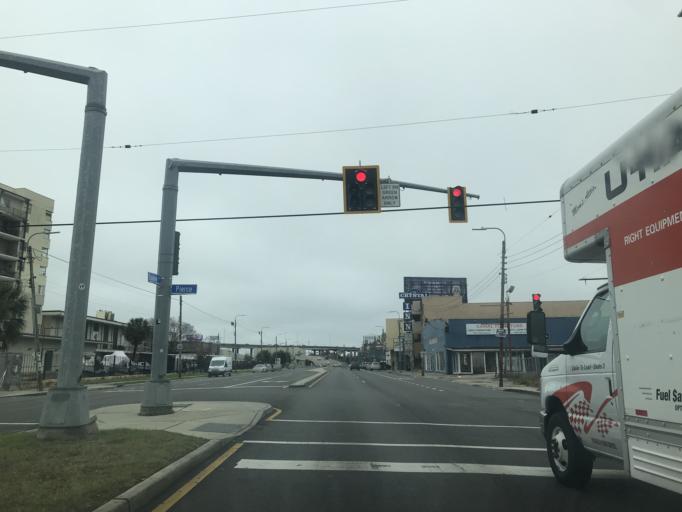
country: US
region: Louisiana
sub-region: Orleans Parish
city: New Orleans
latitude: 29.9680
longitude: -90.1043
